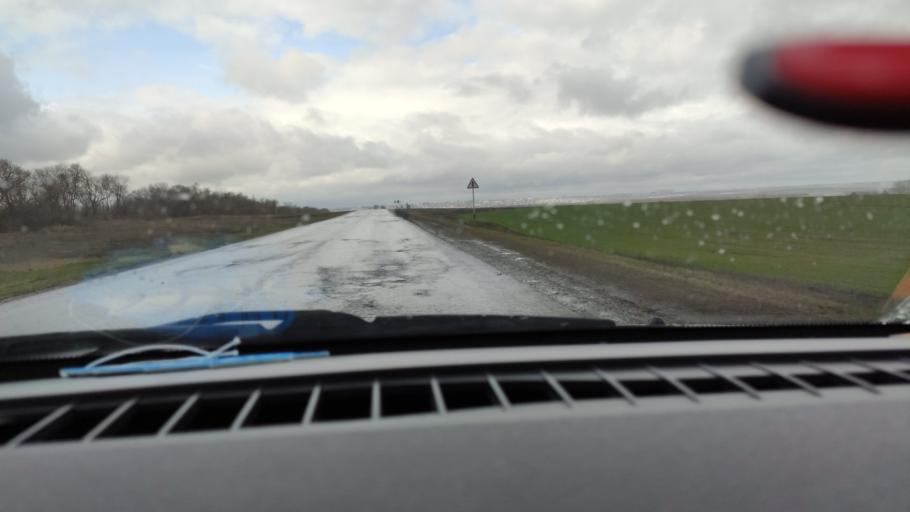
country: RU
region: Samara
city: Koshki
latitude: 54.1956
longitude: 50.5444
